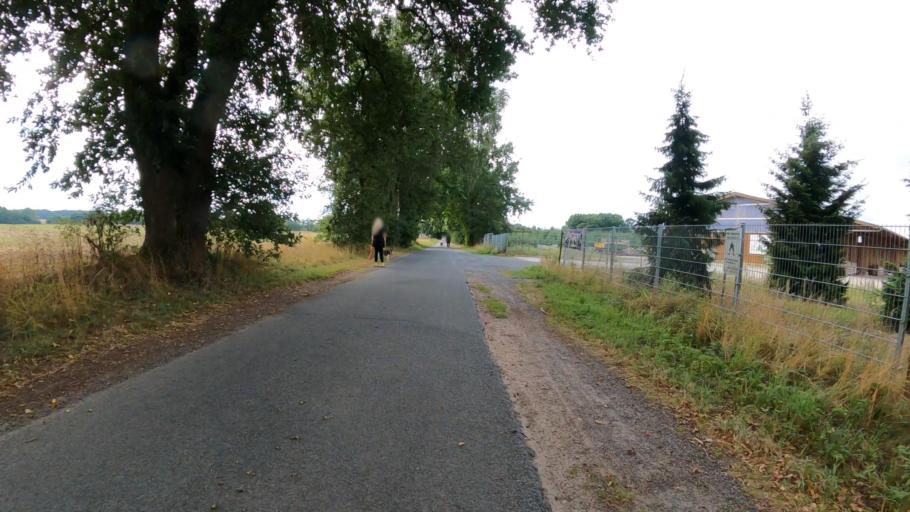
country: DE
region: Lower Saxony
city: Appel
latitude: 53.4016
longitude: 9.7809
